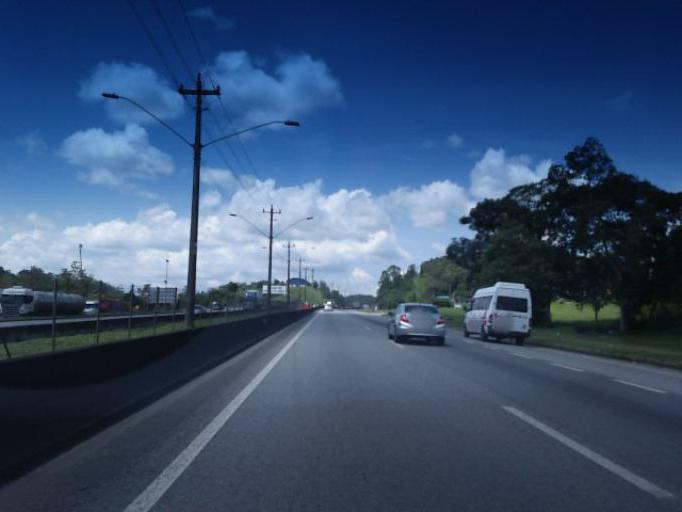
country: BR
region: Sao Paulo
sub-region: Sao Lourenco Da Serra
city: Sao Lourenco da Serra
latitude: -23.8958
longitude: -46.9859
